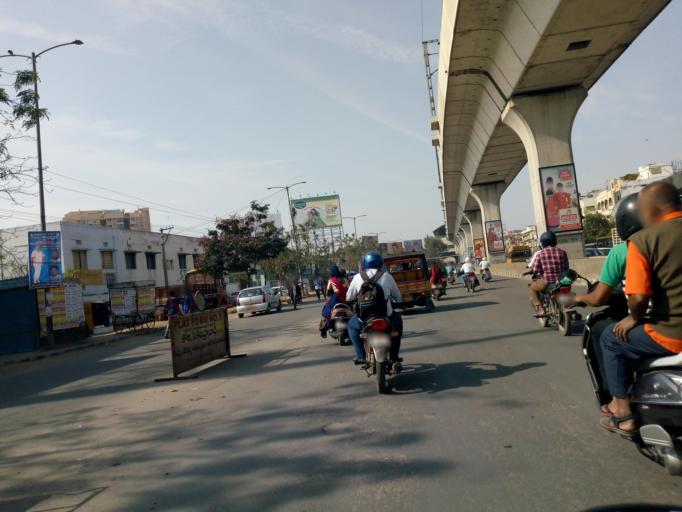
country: IN
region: Telangana
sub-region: Rangareddi
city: Lal Bahadur Nagar
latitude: 17.3473
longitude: 78.5499
